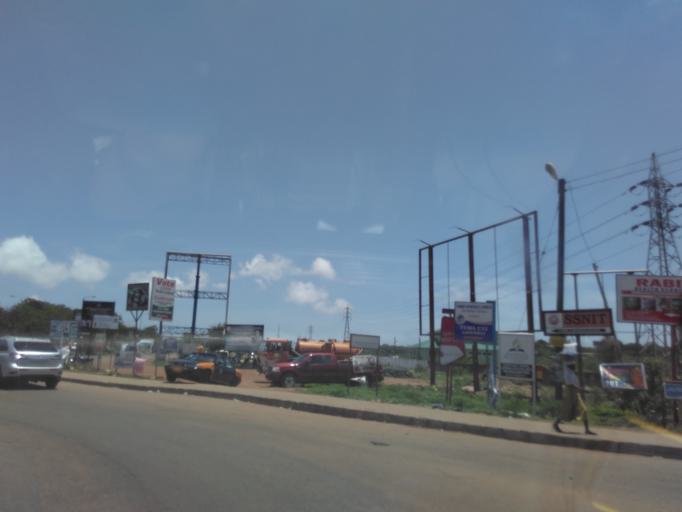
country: GH
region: Greater Accra
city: Tema
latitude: 5.6790
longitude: -0.0231
